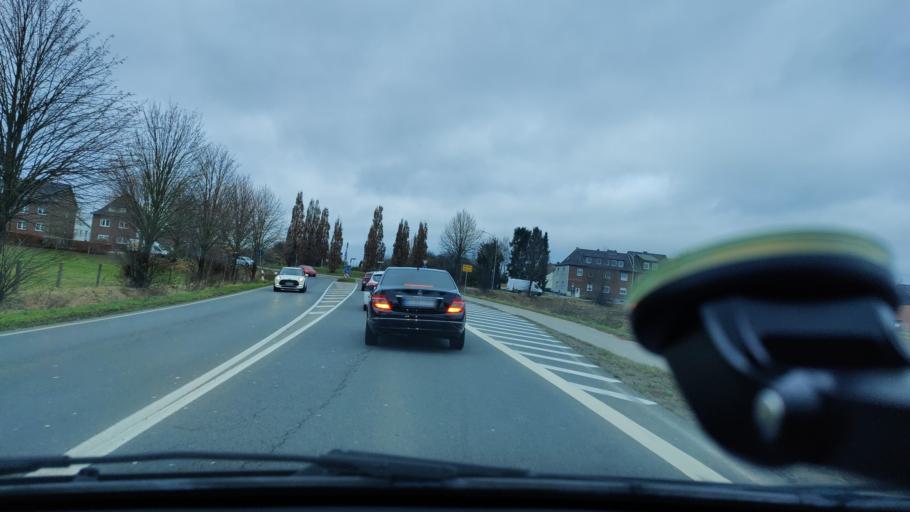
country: DE
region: North Rhine-Westphalia
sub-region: Regierungsbezirk Koln
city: Wurselen
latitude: 50.8311
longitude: 6.1711
